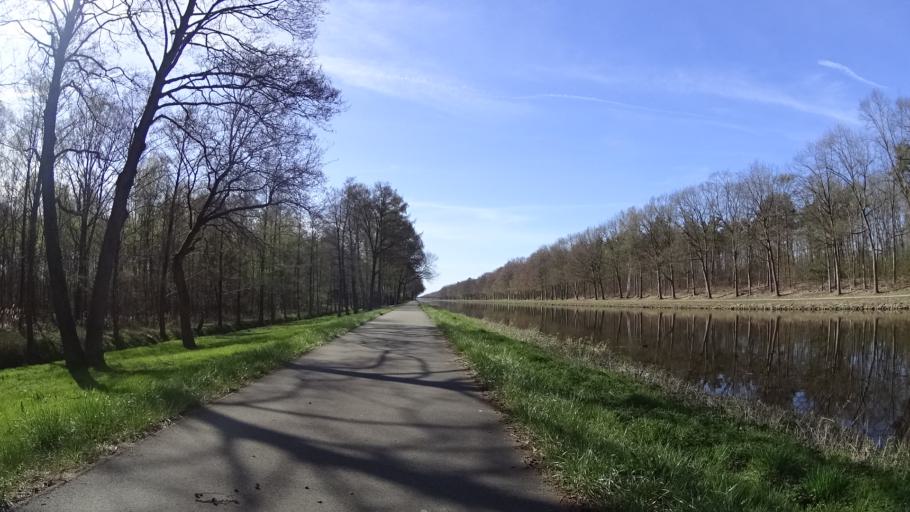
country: DE
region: Lower Saxony
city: Meppen
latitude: 52.6647
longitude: 7.3050
